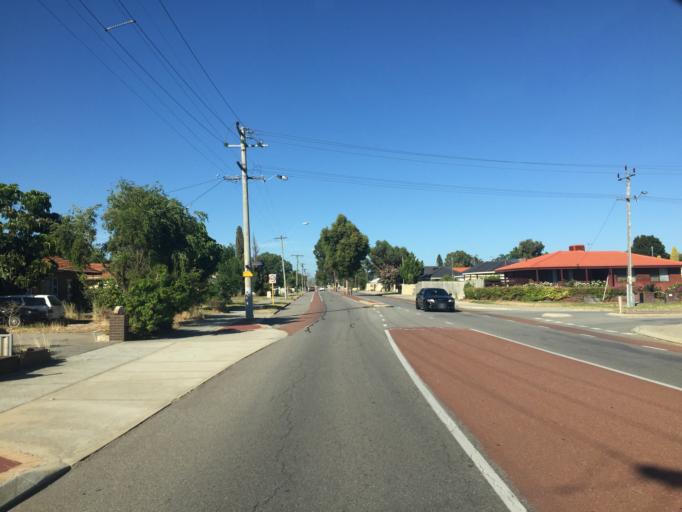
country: AU
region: Western Australia
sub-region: Canning
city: East Cannington
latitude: -32.0177
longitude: 115.9605
